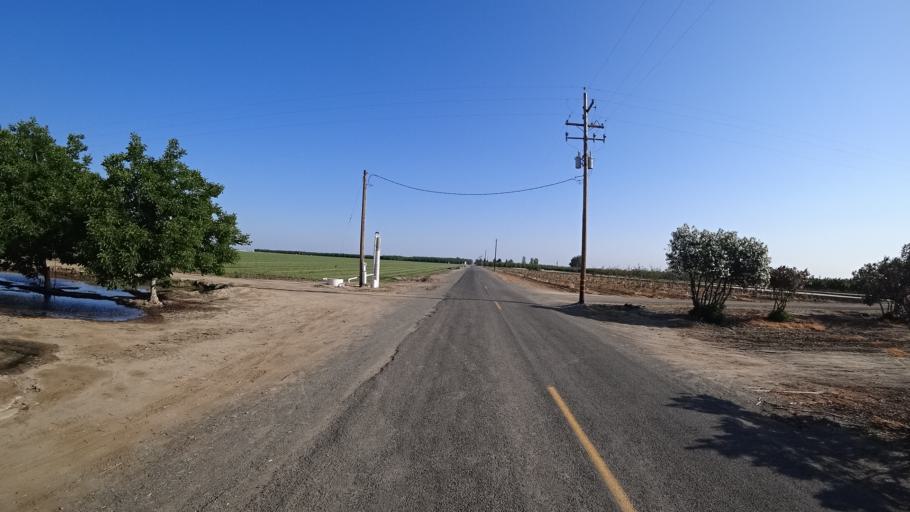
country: US
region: California
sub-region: Kings County
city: Home Garden
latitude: 36.2767
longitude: -119.5652
